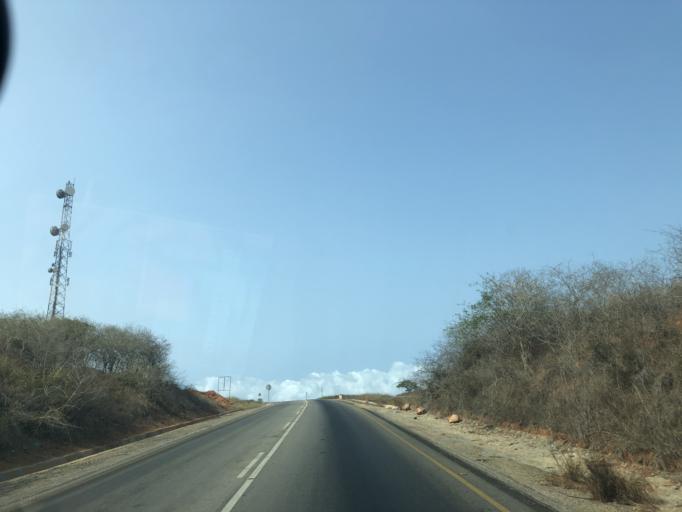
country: AO
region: Luanda
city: Luanda
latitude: -9.6924
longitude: 13.2126
